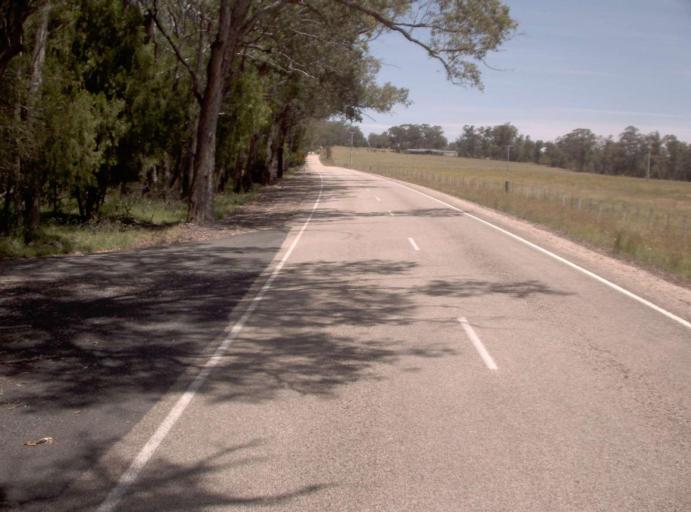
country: AU
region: Victoria
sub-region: East Gippsland
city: Lakes Entrance
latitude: -37.6783
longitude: 147.8500
